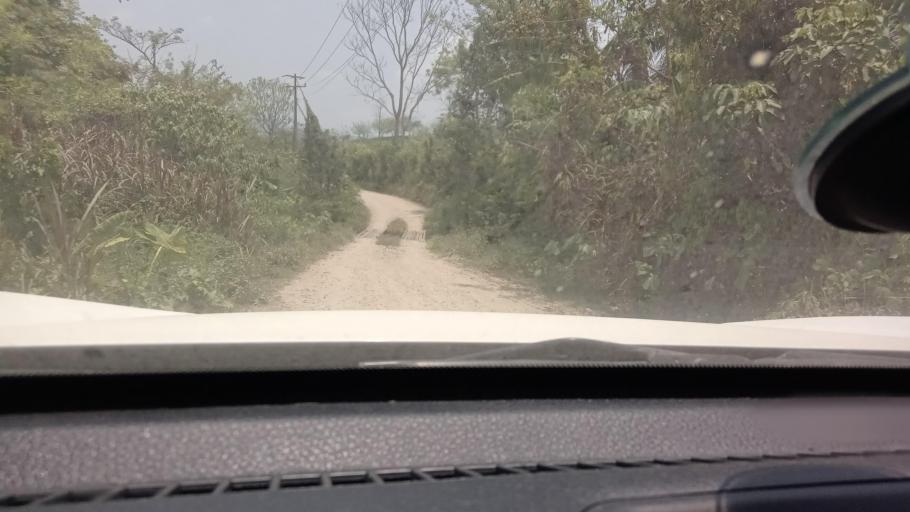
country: MX
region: Tabasco
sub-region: Huimanguillo
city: Francisco Rueda
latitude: 17.4841
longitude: -93.9404
